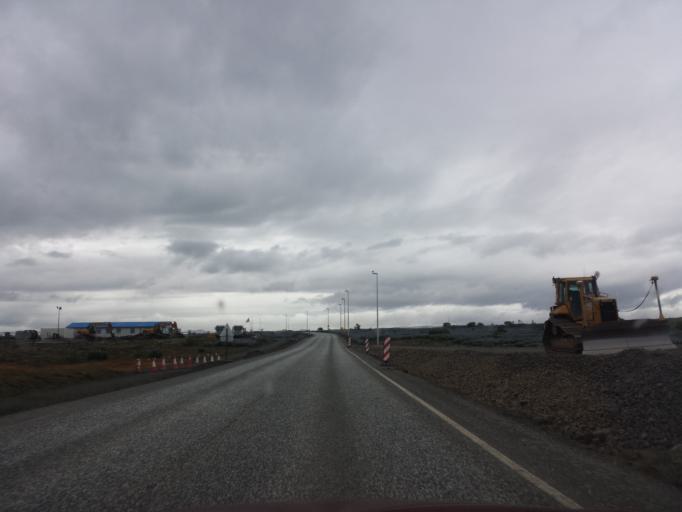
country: IS
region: Capital Region
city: Alftanes
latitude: 64.0913
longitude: -21.9877
